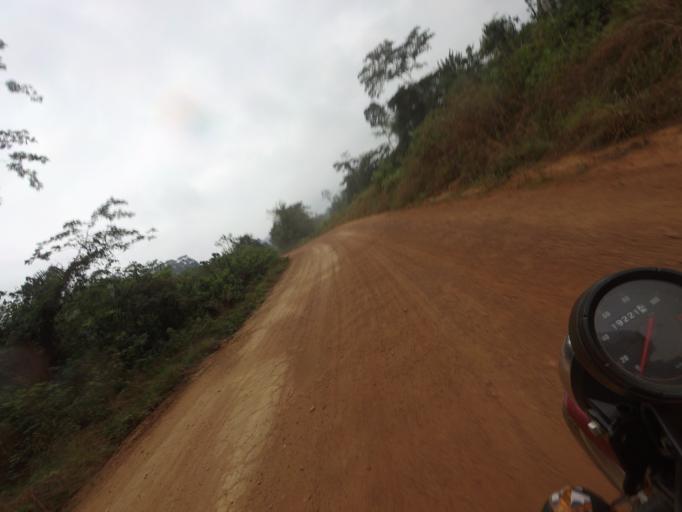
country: LR
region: Nimba
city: Sanniquellie
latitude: 7.4157
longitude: -8.6518
